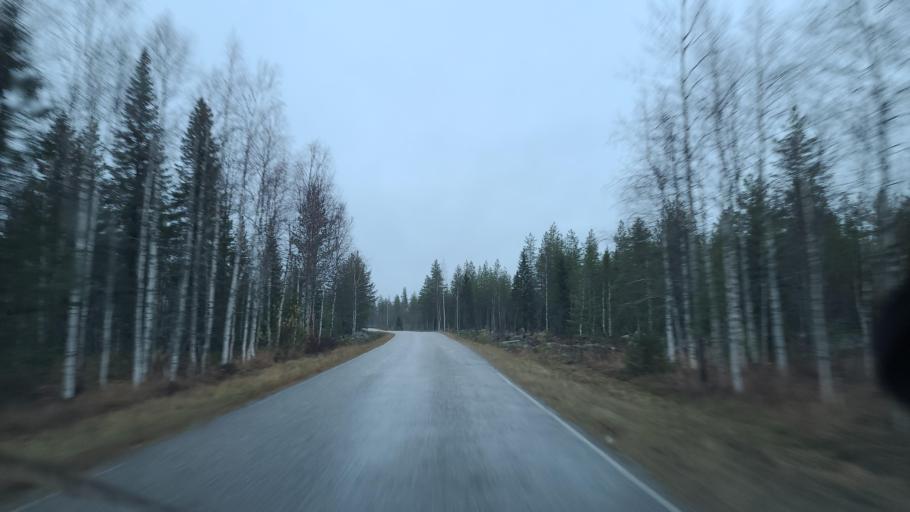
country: FI
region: Lapland
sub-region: Kemi-Tornio
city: Simo
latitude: 65.9243
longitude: 25.2021
